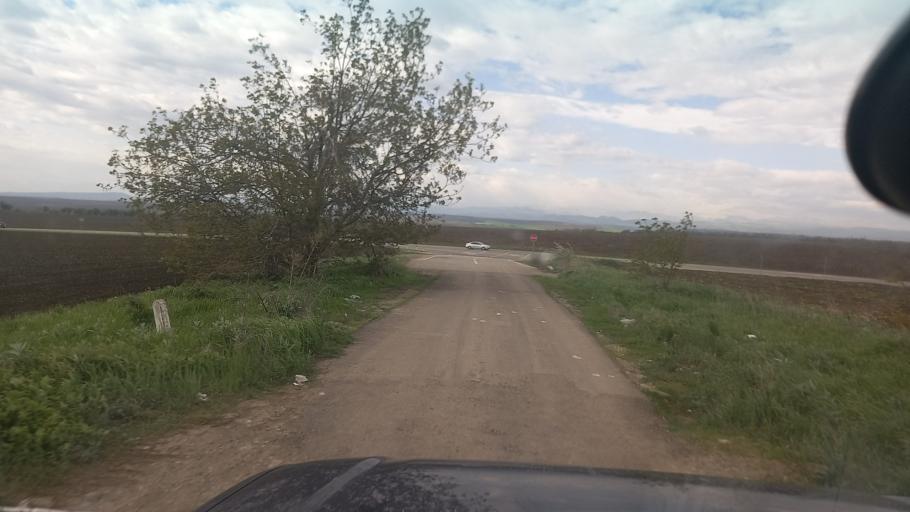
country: RU
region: Kabardino-Balkariya
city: Kuba-Taba
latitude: 43.7942
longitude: 43.3950
